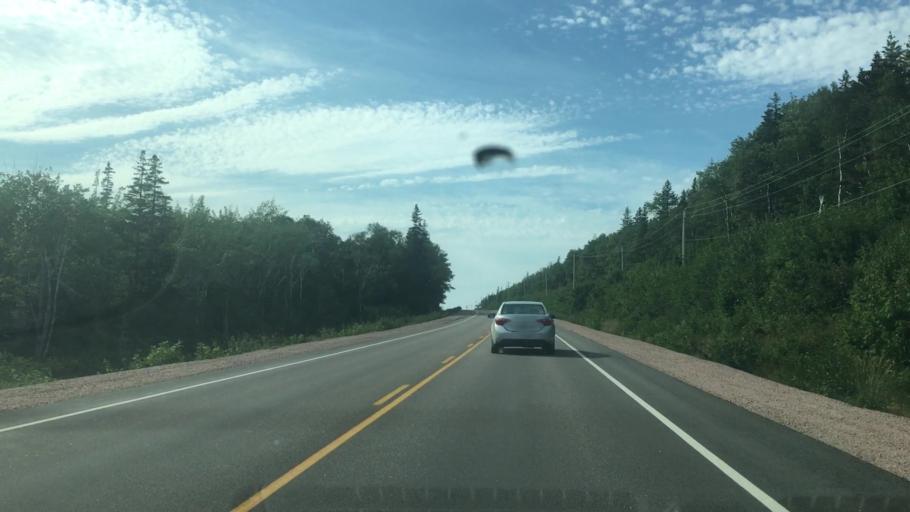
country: CA
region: Nova Scotia
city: Sydney Mines
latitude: 46.8172
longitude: -60.3458
